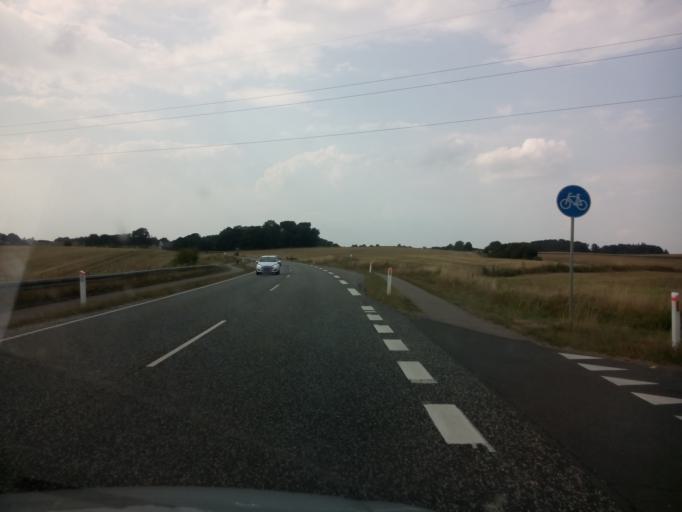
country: DK
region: Central Jutland
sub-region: Skanderborg Kommune
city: Skanderborg
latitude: 56.0494
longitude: 9.8834
